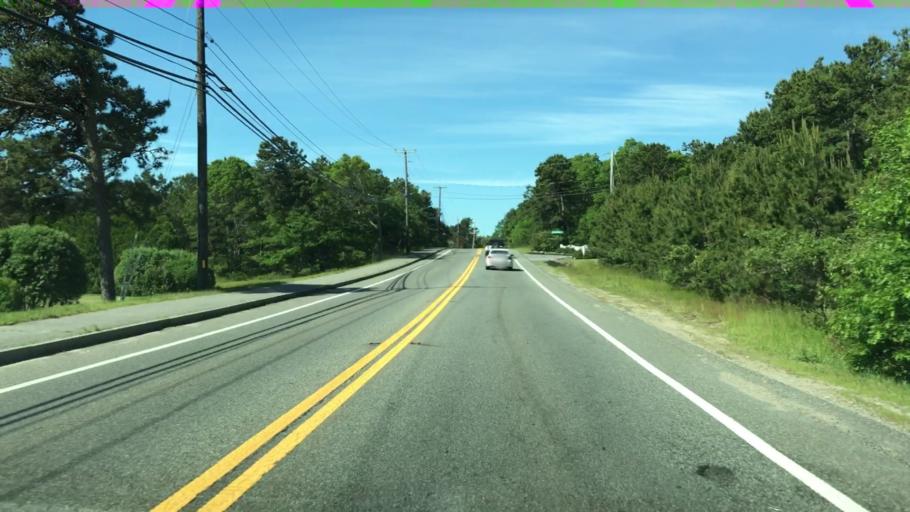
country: US
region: Massachusetts
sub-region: Barnstable County
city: Mashpee
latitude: 41.6069
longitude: -70.4934
